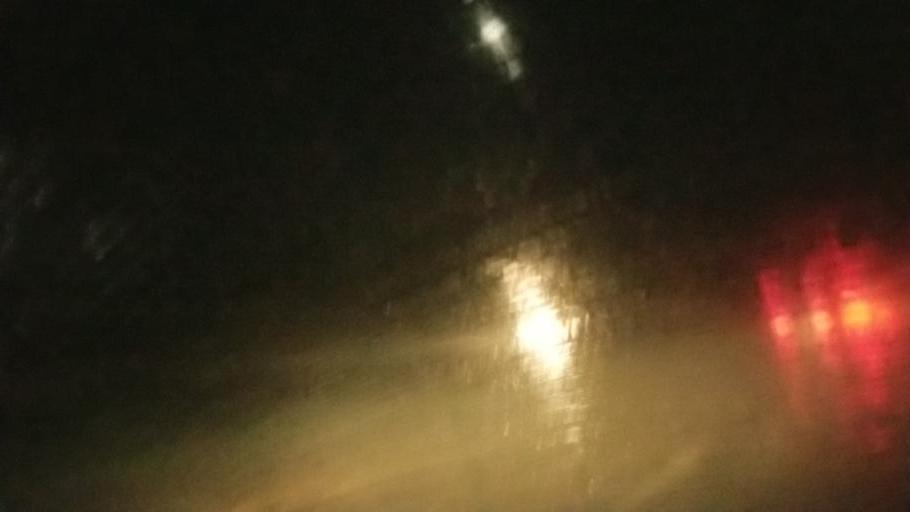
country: US
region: New York
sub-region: Seneca County
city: Waterloo
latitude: 42.9661
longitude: -76.8619
